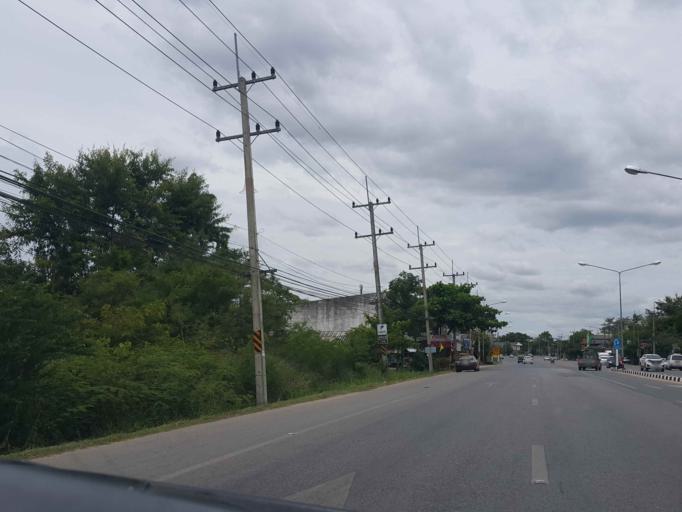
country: TH
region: Chiang Mai
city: San Pa Tong
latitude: 18.5696
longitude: 98.8770
